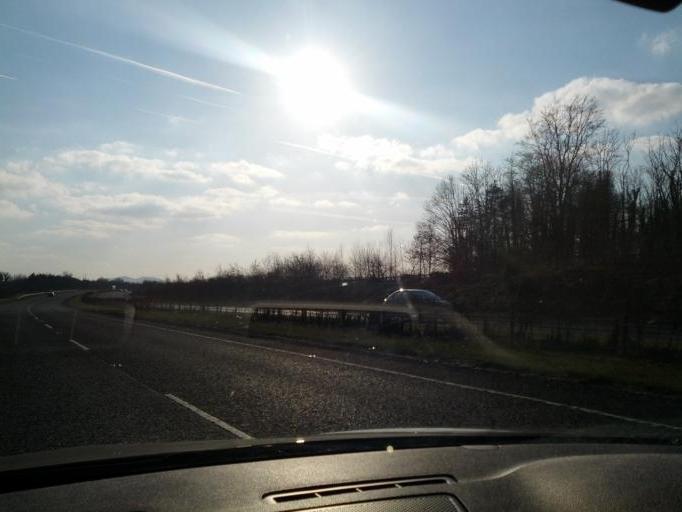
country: IE
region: Leinster
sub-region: Kildare
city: Monasterevin
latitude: 53.1186
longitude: -7.0442
